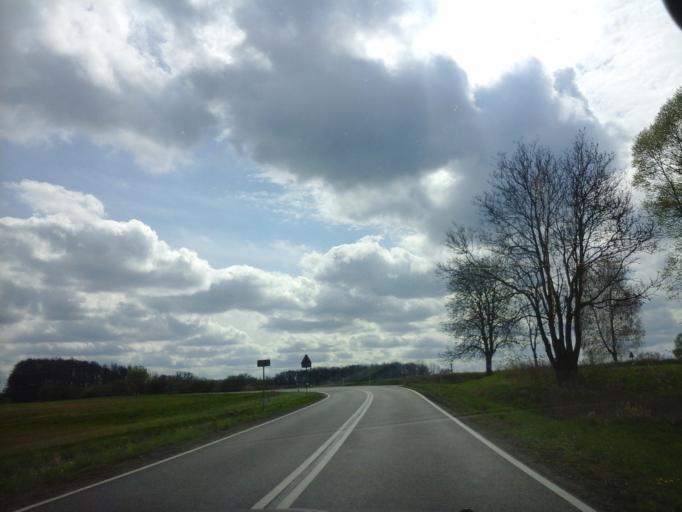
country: PL
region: West Pomeranian Voivodeship
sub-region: Powiat choszczenski
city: Pelczyce
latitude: 53.1136
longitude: 15.3438
